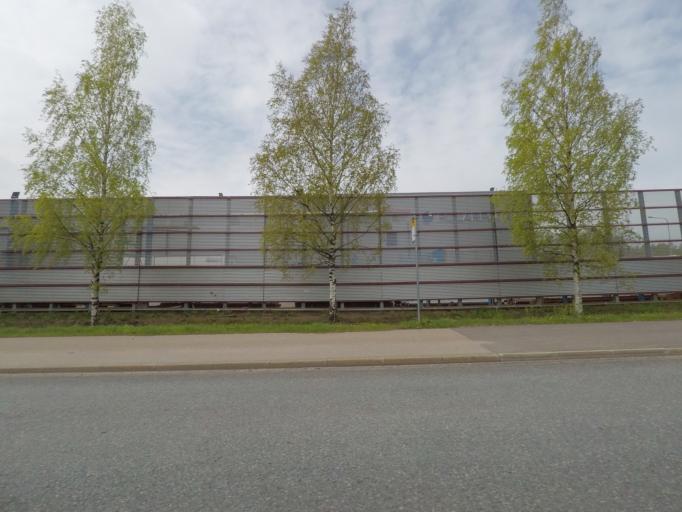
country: FI
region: Uusimaa
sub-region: Helsinki
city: Vantaa
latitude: 60.2959
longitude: 24.9955
